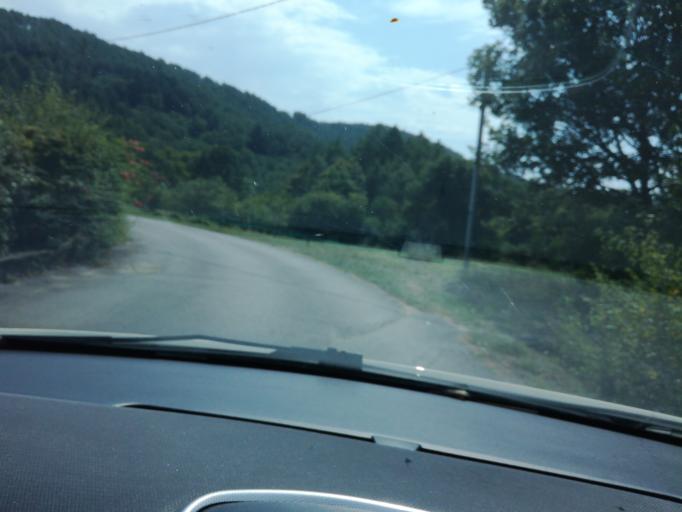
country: FR
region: Rhone-Alpes
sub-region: Departement de l'Ardeche
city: Labegude
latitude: 44.6313
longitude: 4.3624
